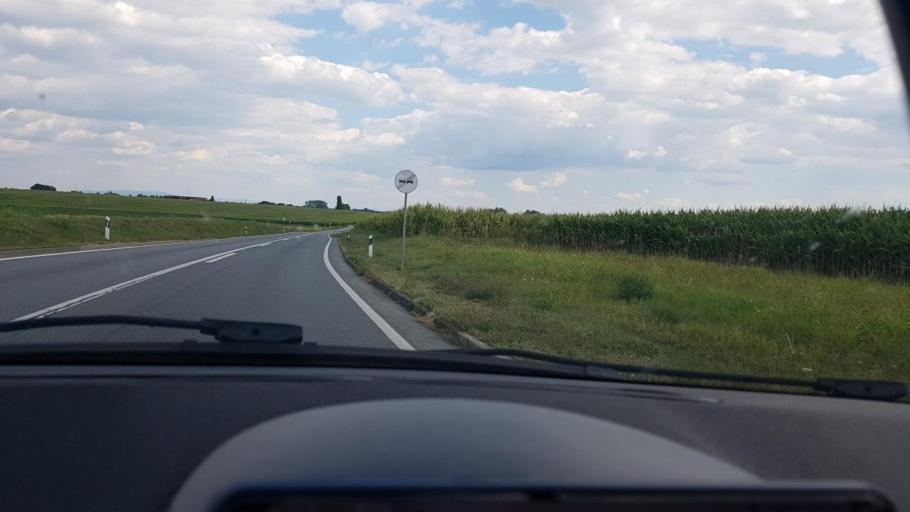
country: HR
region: Bjelovarsko-Bilogorska
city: Zdralovi
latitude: 45.8512
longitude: 16.9398
